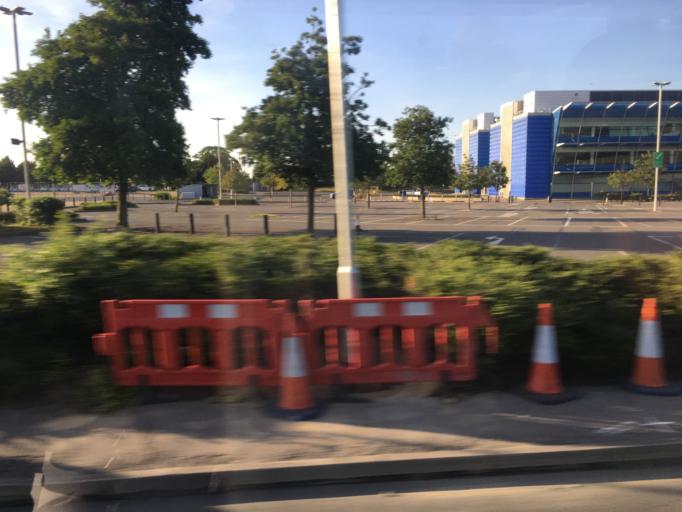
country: GB
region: England
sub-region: Greater London
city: West Drayton
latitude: 51.4802
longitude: -0.4706
